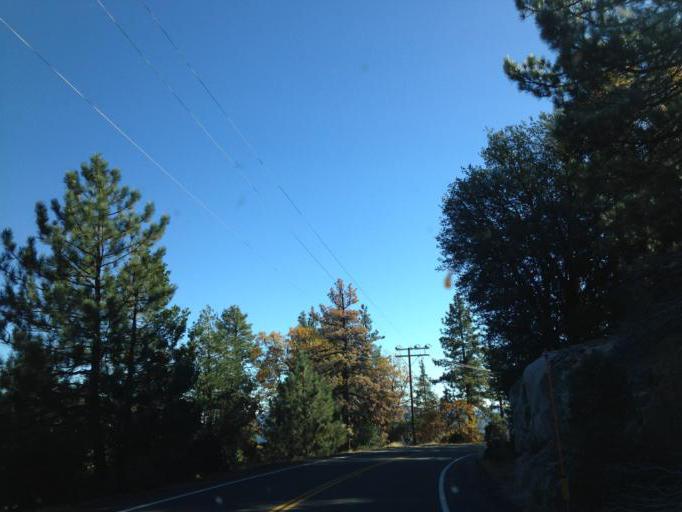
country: US
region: California
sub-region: Riverside County
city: Idyllwild-Pine Cove
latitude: 33.7509
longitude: -116.7350
